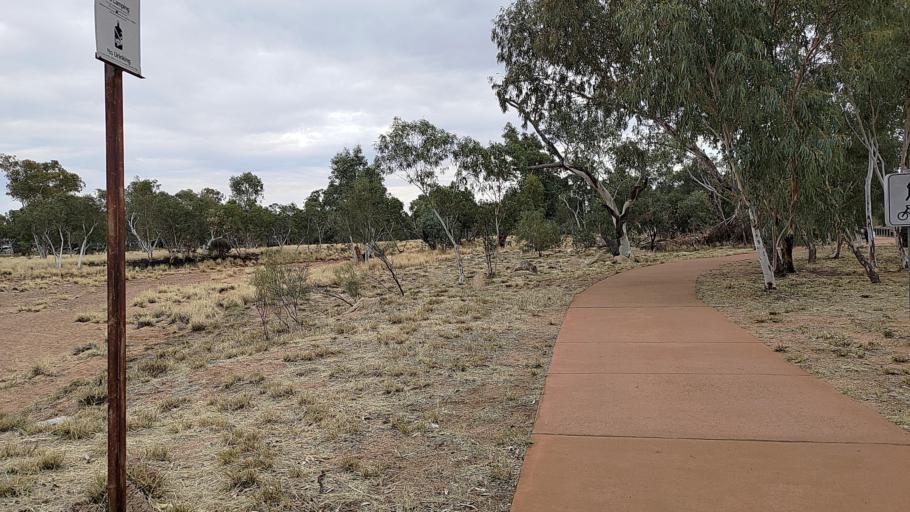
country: AU
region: Northern Territory
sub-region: Alice Springs
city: Alice Springs
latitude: -23.7131
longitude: 133.8794
